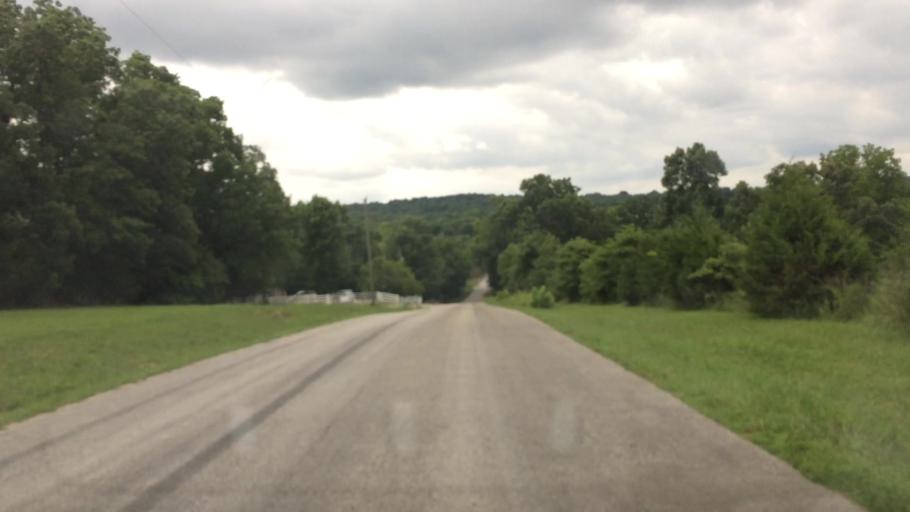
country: US
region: Missouri
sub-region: Webster County
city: Marshfield
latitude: 37.3075
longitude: -92.9846
